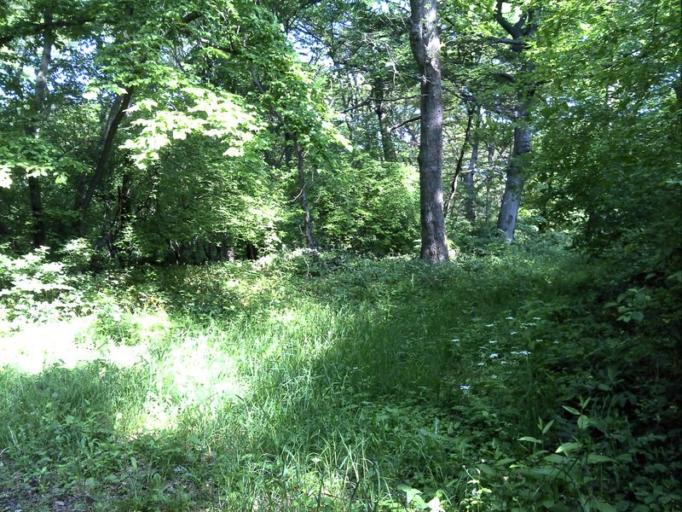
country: HU
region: Baranya
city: Pecs
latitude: 46.1120
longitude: 18.1749
